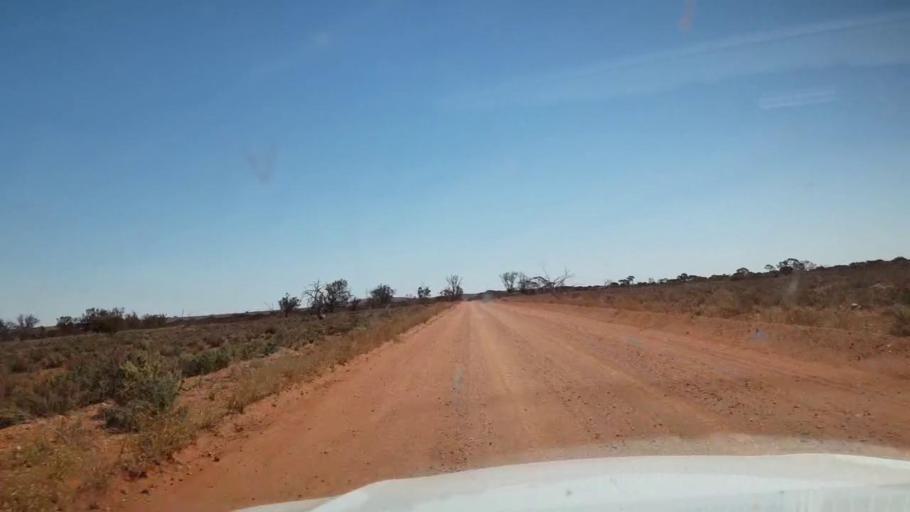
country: AU
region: South Australia
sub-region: Whyalla
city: Whyalla
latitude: -32.6845
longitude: 137.1039
